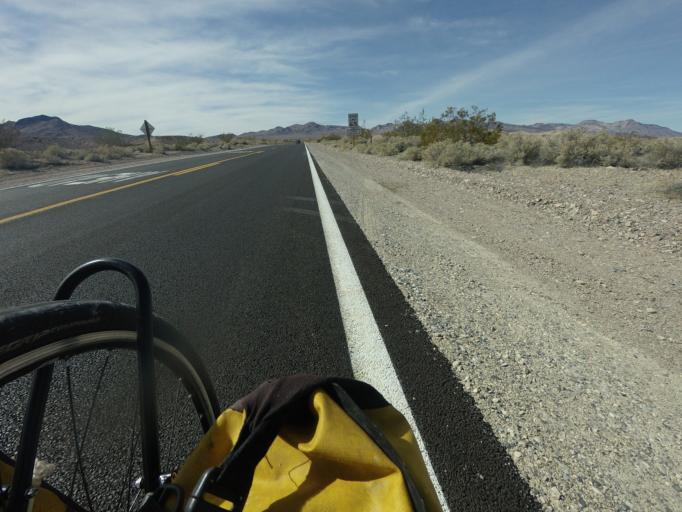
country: US
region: Nevada
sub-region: Nye County
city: Pahrump
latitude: 35.9967
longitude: -116.2792
